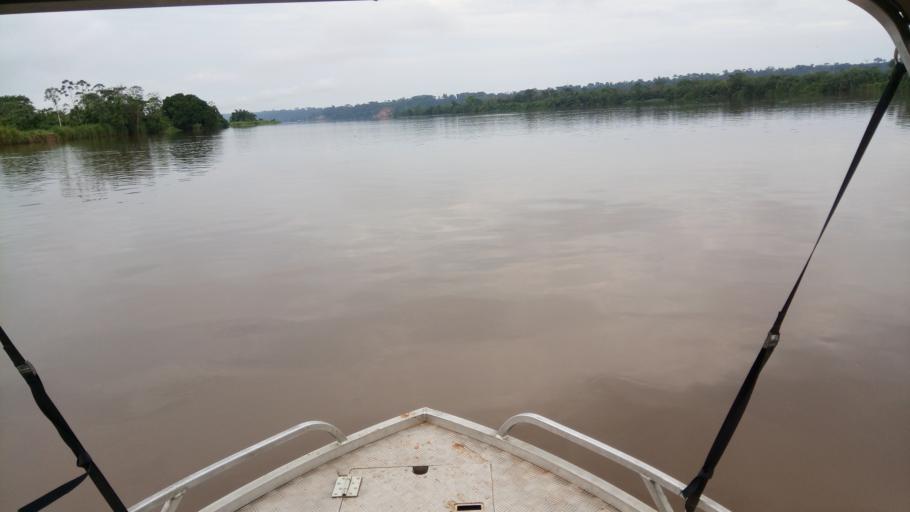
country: CD
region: Eastern Province
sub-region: Sous-Region de la Tshopo
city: Yangambi
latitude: 0.7359
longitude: 24.5192
